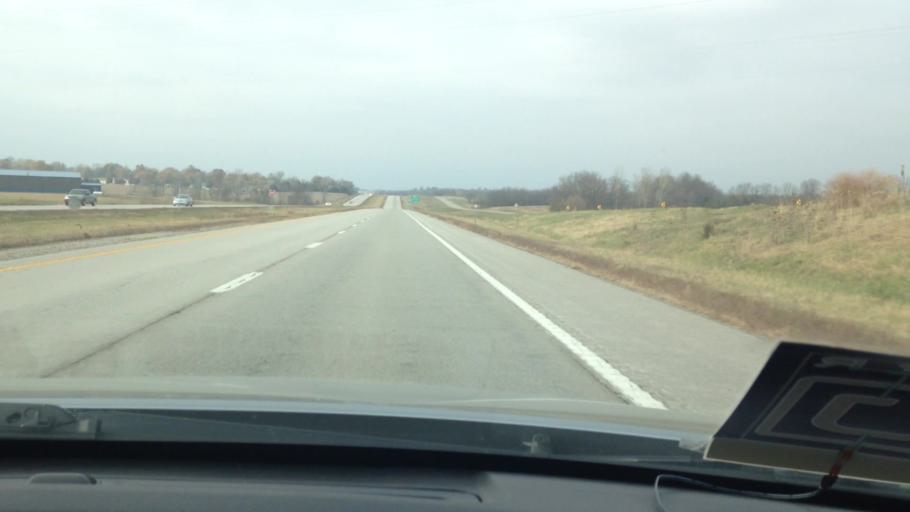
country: US
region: Missouri
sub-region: Cass County
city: Garden City
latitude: 38.5550
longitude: -94.1788
